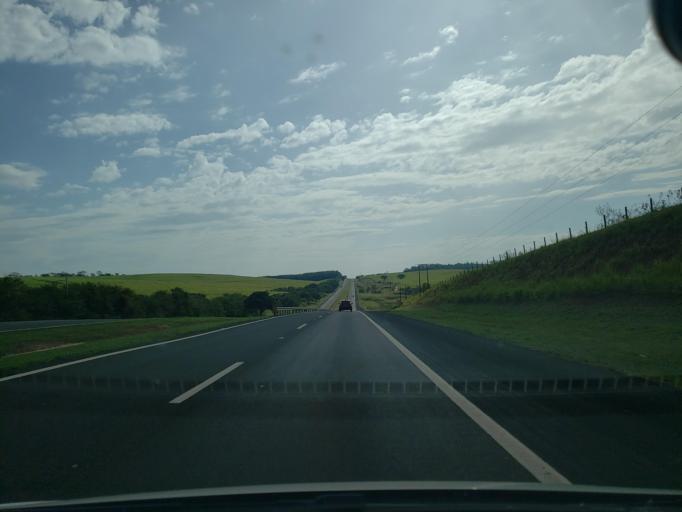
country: BR
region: Sao Paulo
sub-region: Lins
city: Lins
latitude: -21.7342
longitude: -49.7070
